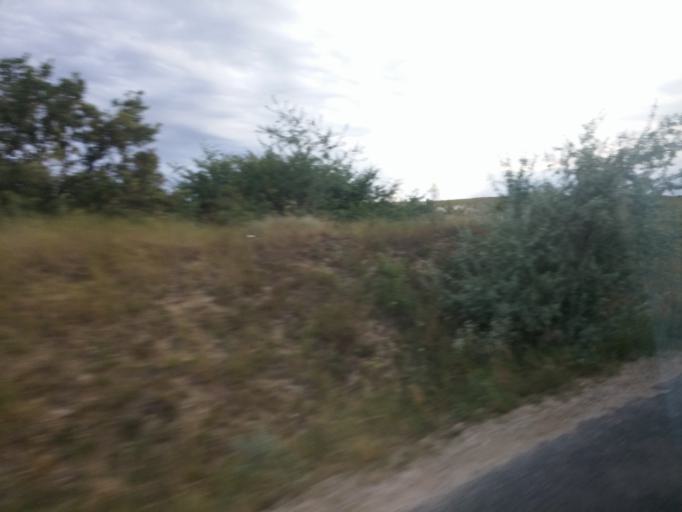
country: HU
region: Veszprem
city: Varpalota
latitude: 47.2203
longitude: 18.1474
